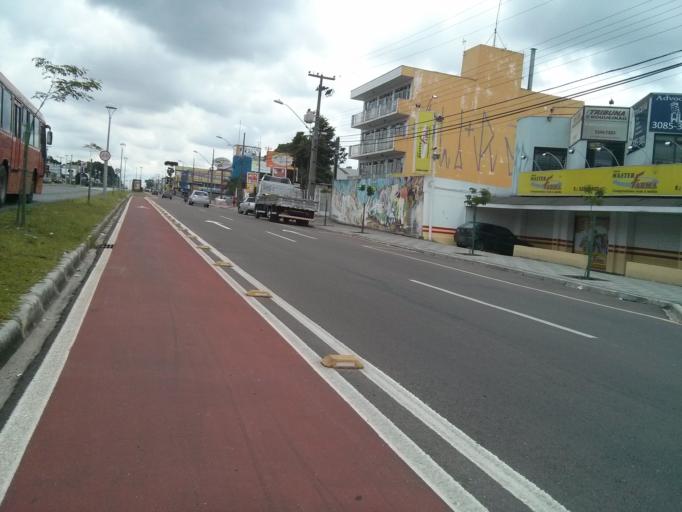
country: BR
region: Parana
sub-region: Sao Jose Dos Pinhais
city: Sao Jose dos Pinhais
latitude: -25.5140
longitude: -49.2314
